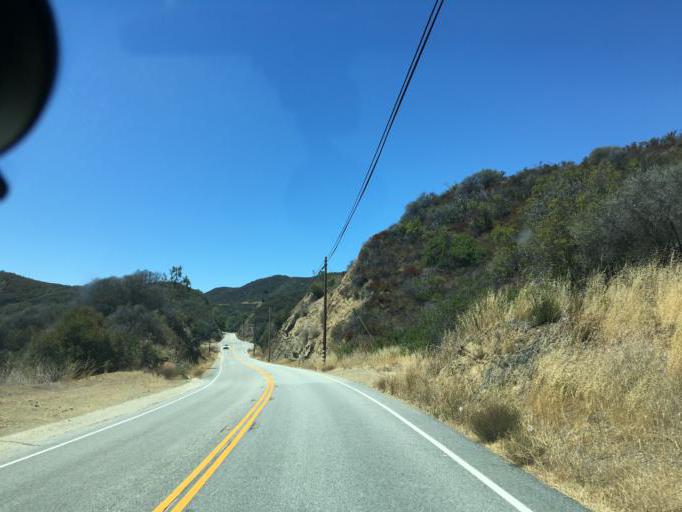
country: US
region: California
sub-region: Los Angeles County
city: Westlake Village
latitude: 34.0875
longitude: -118.8520
